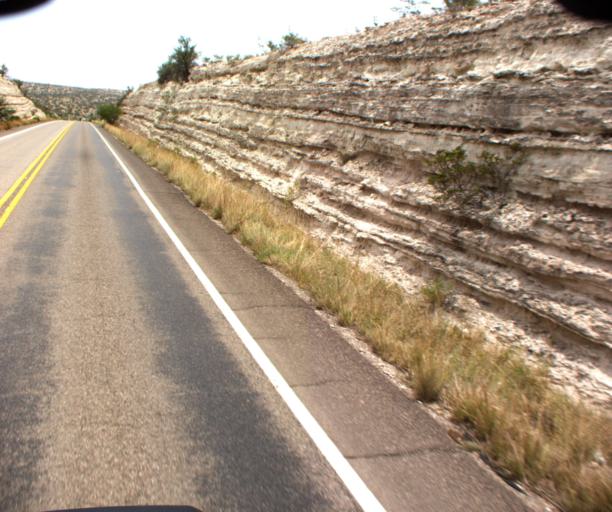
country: US
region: Arizona
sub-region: Gila County
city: Peridot
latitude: 33.2690
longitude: -110.3154
